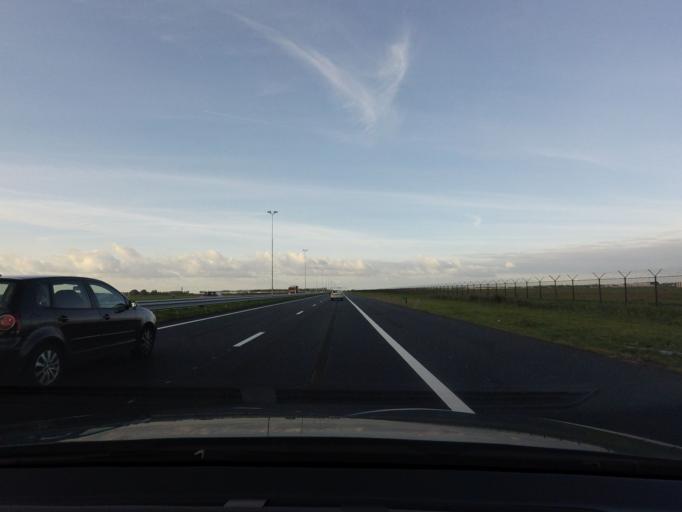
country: NL
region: North Holland
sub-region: Gemeente Haarlemmermeer
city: Hoofddorp
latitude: 52.3069
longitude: 4.7321
